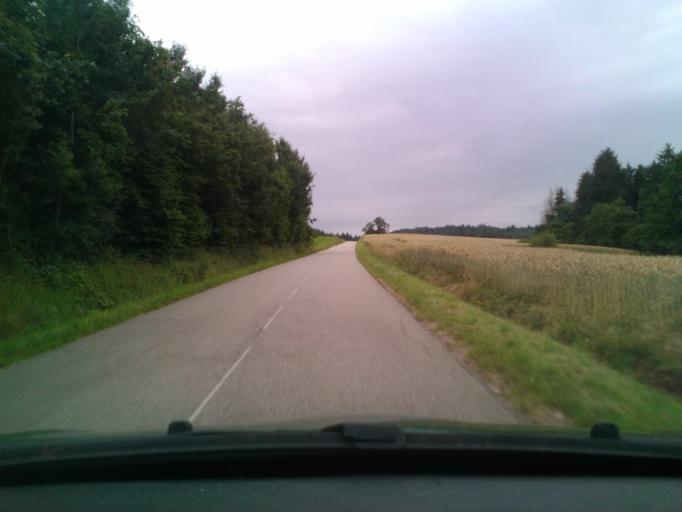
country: FR
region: Lorraine
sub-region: Departement des Vosges
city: Bruyeres
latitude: 48.2181
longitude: 6.7558
